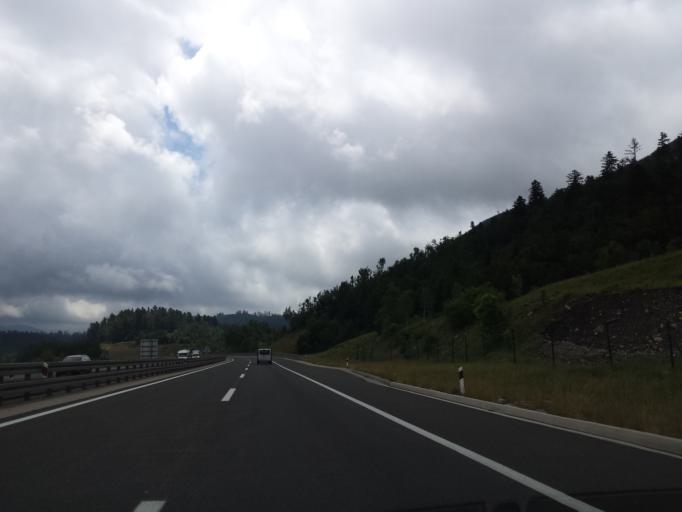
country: HR
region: Primorsko-Goranska
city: Hreljin
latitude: 45.3219
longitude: 14.6633
